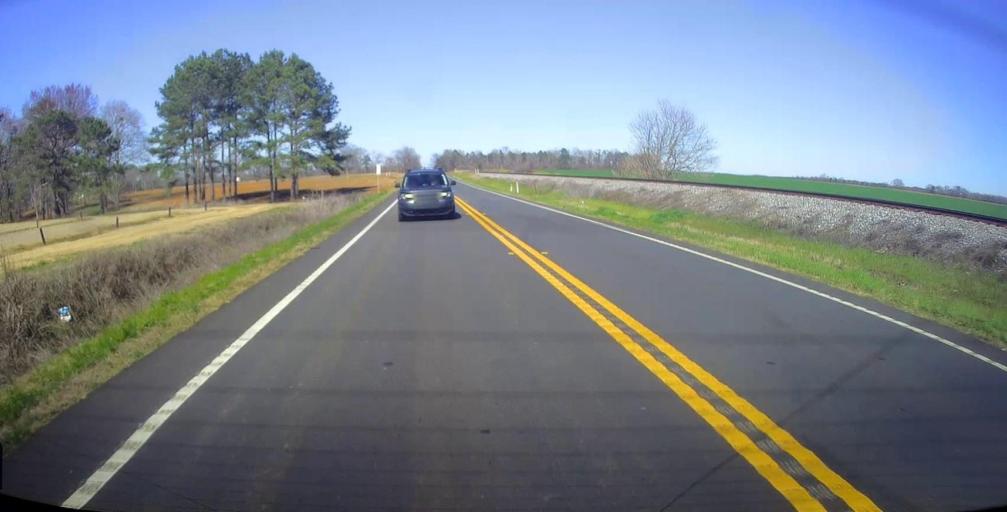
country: US
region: Georgia
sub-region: Macon County
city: Marshallville
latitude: 32.4722
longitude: -83.9353
